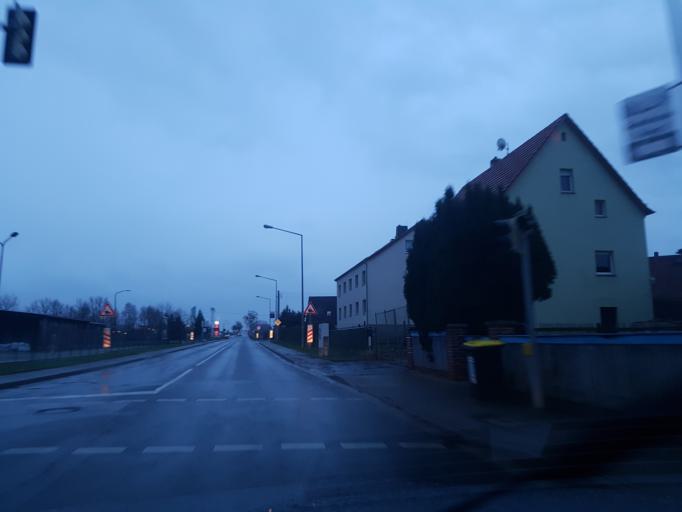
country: DE
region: Saxony
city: Grossenhain
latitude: 51.2816
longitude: 13.5208
